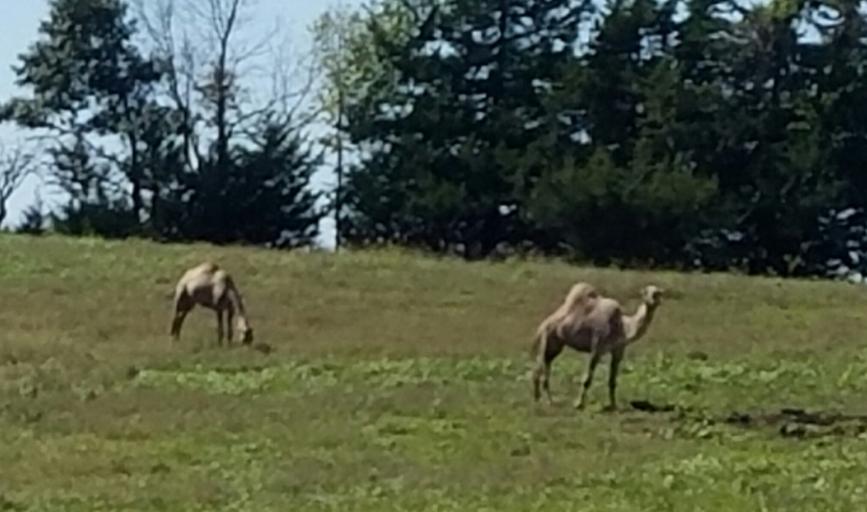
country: US
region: Missouri
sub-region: Worth County
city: Grant City
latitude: 40.4183
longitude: -94.4050
